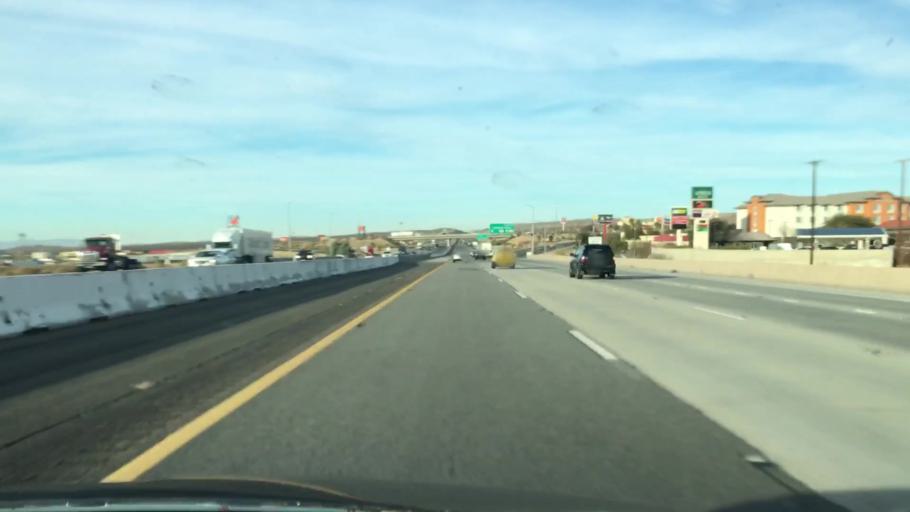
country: US
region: California
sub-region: San Bernardino County
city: Lenwood
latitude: 34.8480
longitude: -117.0865
